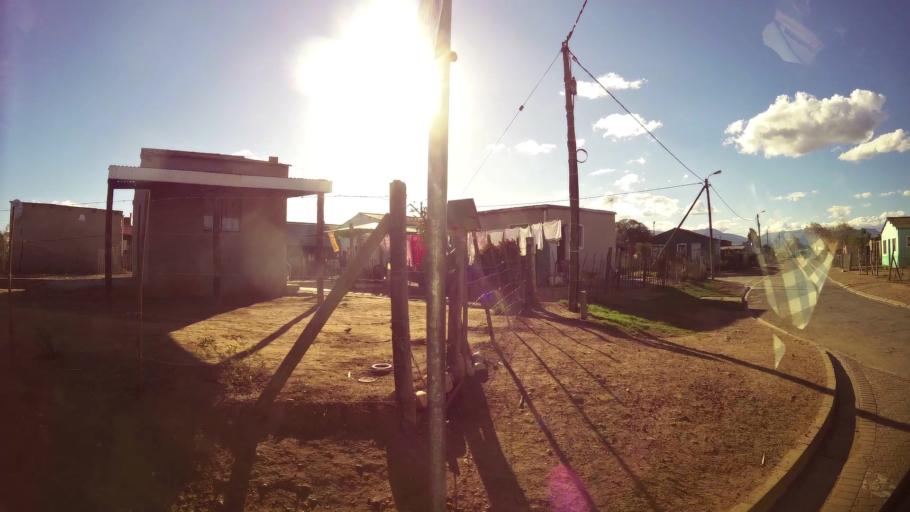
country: ZA
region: Western Cape
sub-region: Eden District Municipality
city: Riversdale
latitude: -34.1078
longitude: 20.9613
